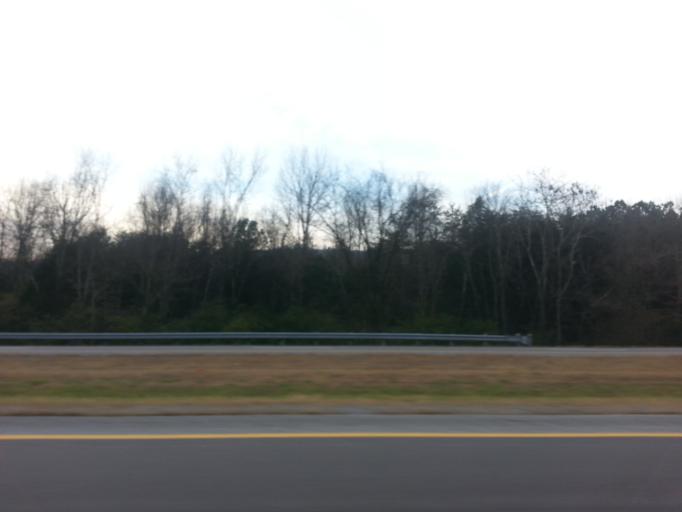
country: US
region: Tennessee
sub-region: Rhea County
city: Spring City
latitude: 35.6291
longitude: -84.9007
